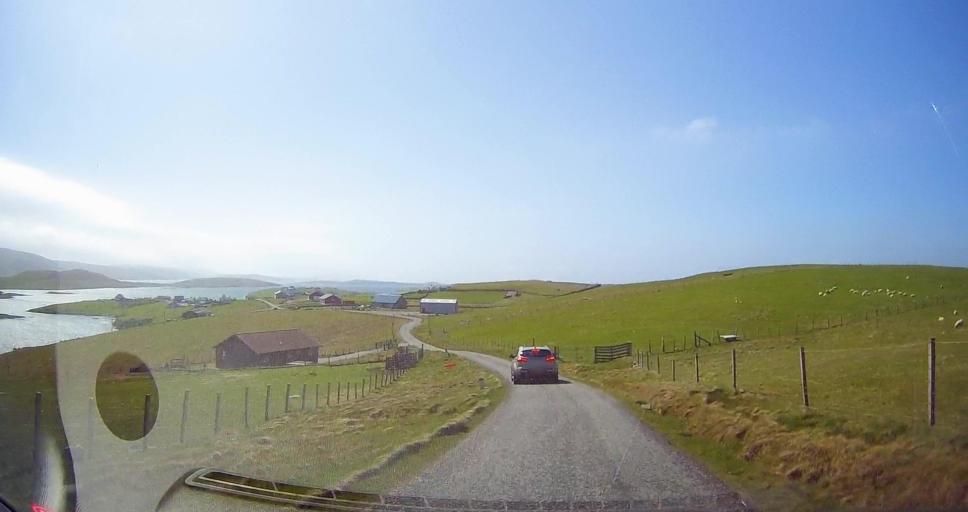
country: GB
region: Scotland
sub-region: Shetland Islands
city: Sandwick
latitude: 60.0735
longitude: -1.3396
